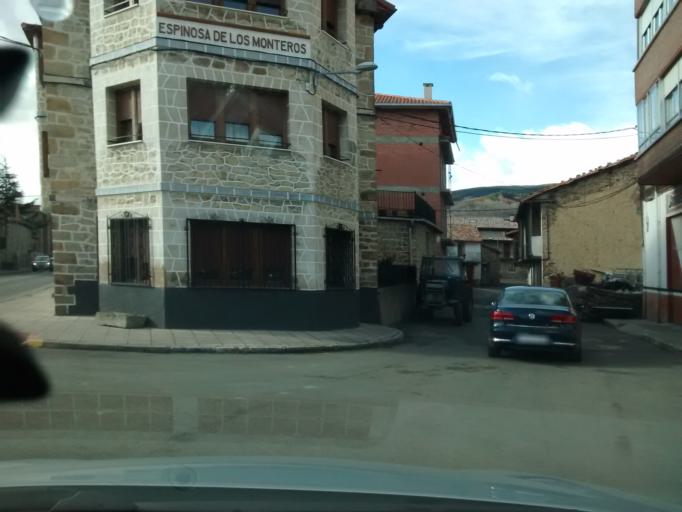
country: ES
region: Castille and Leon
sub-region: Provincia de Burgos
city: Espinosa de los Monteros
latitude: 43.0757
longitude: -3.5461
